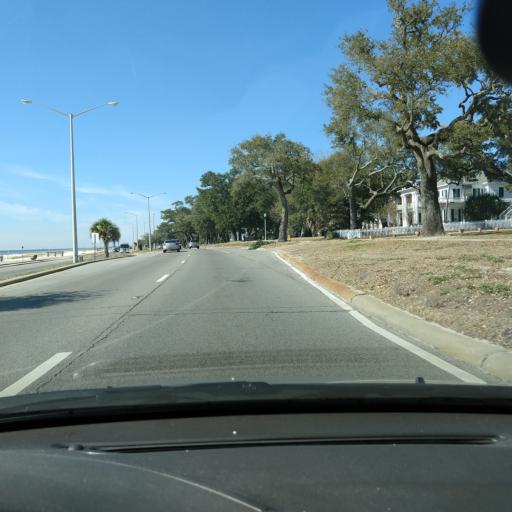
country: US
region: Mississippi
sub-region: Harrison County
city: Biloxi
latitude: 30.3949
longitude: -88.9152
